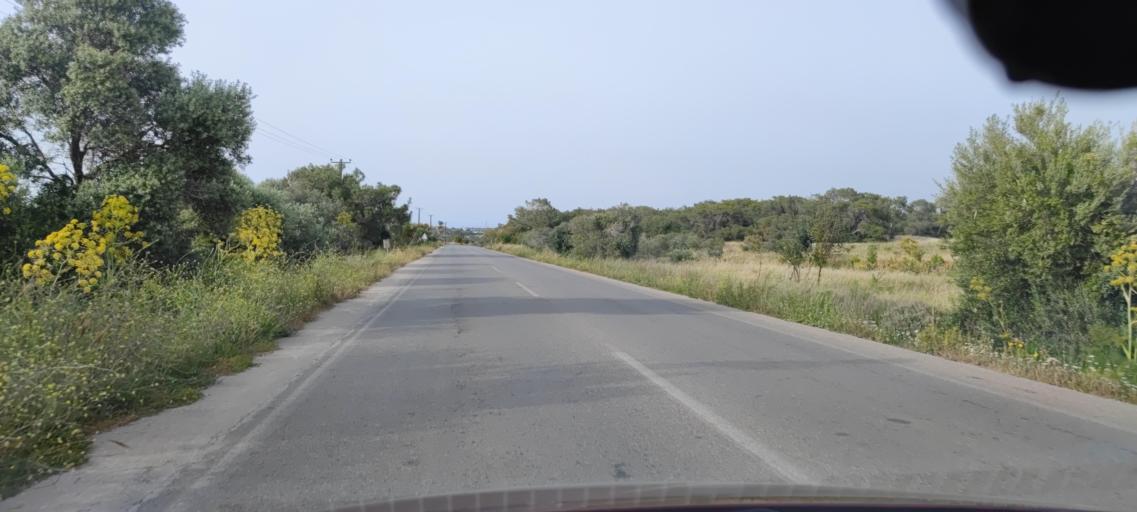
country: CY
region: Ammochostos
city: Leonarisso
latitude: 35.4864
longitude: 34.1514
